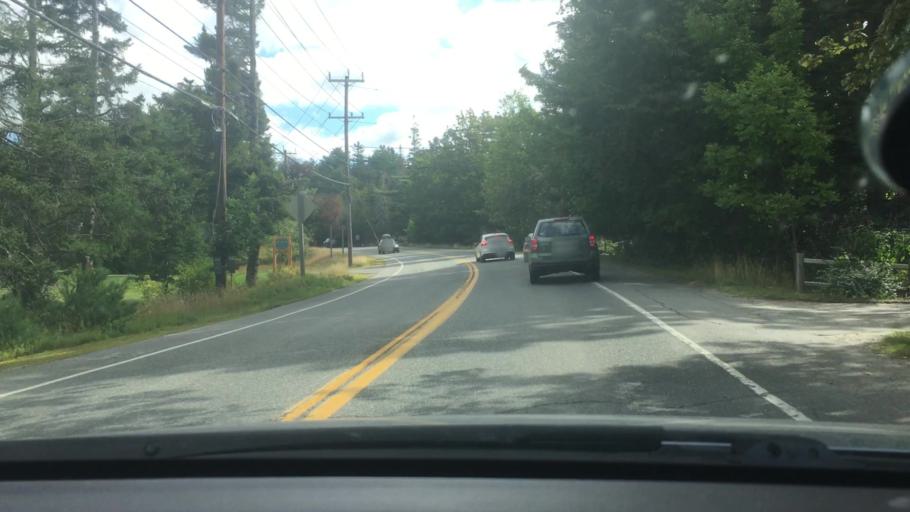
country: US
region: Maine
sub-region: Hancock County
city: Trenton
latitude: 44.3691
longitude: -68.3284
